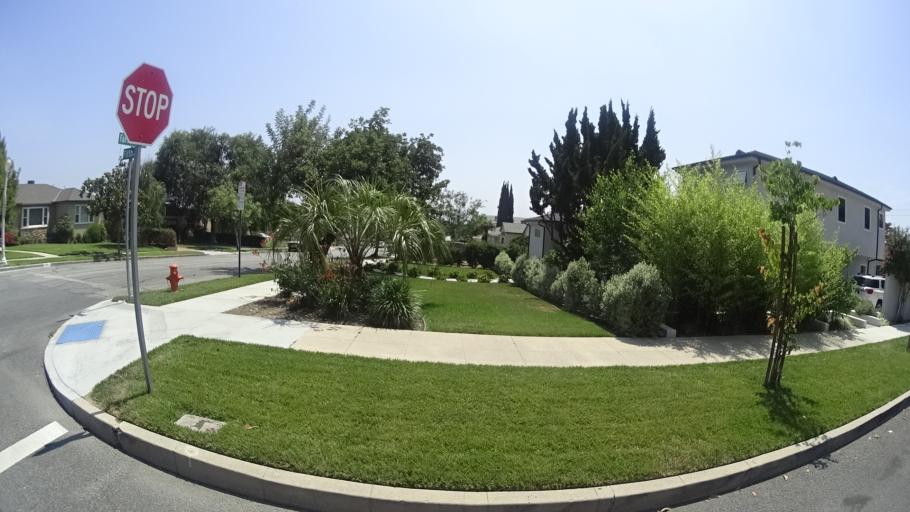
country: US
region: California
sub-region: Los Angeles County
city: Burbank
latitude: 34.1902
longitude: -118.3131
